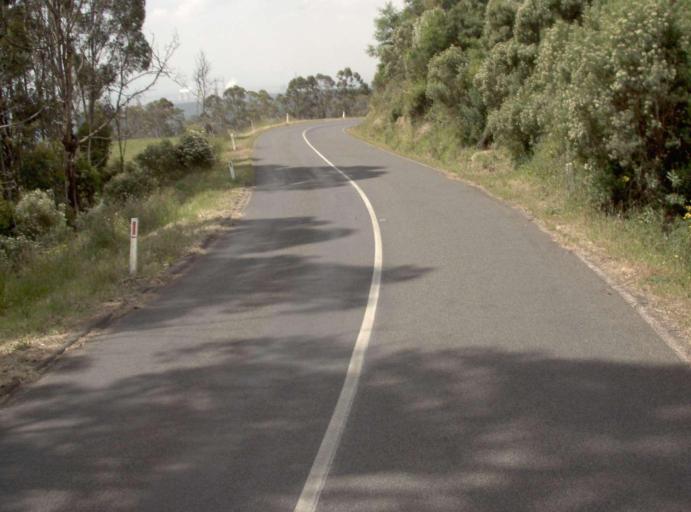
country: AU
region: Victoria
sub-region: Latrobe
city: Traralgon
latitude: -38.3464
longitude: 146.5686
